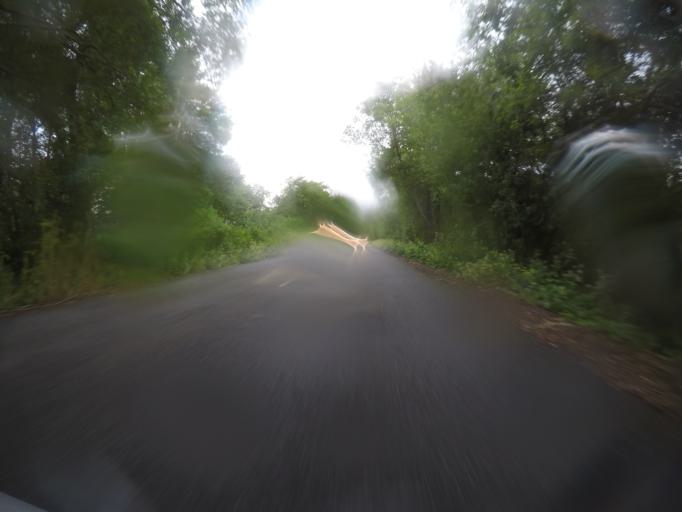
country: US
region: California
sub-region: Humboldt County
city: Westhaven-Moonstone
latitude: 41.3002
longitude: -124.0424
